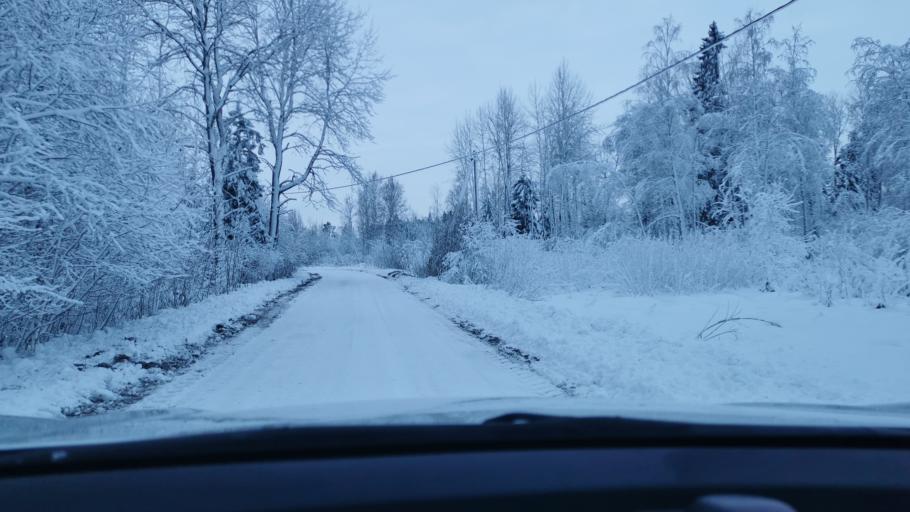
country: EE
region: Laeaene-Virumaa
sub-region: Someru vald
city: Someru
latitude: 59.4802
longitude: 26.4089
